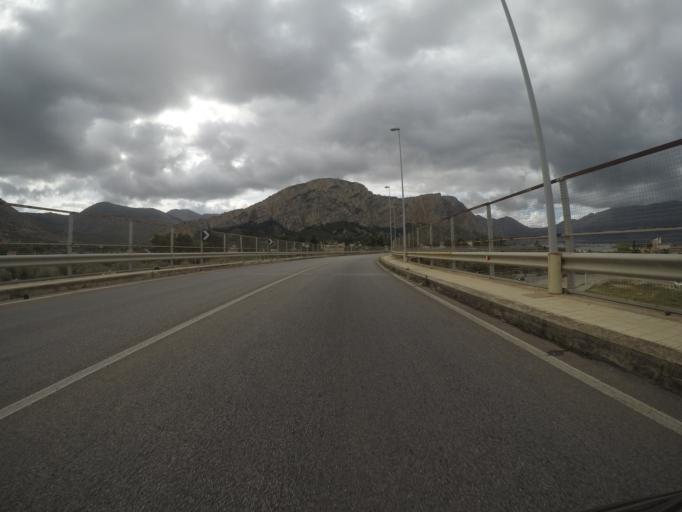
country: IT
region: Sicily
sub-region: Palermo
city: Capaci
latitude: 38.1674
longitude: 13.2219
